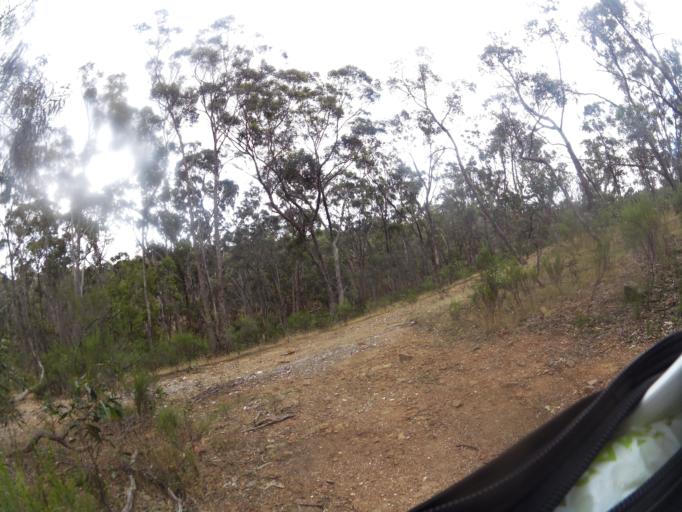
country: AU
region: Victoria
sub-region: Mount Alexander
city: Castlemaine
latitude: -37.0708
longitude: 144.2556
